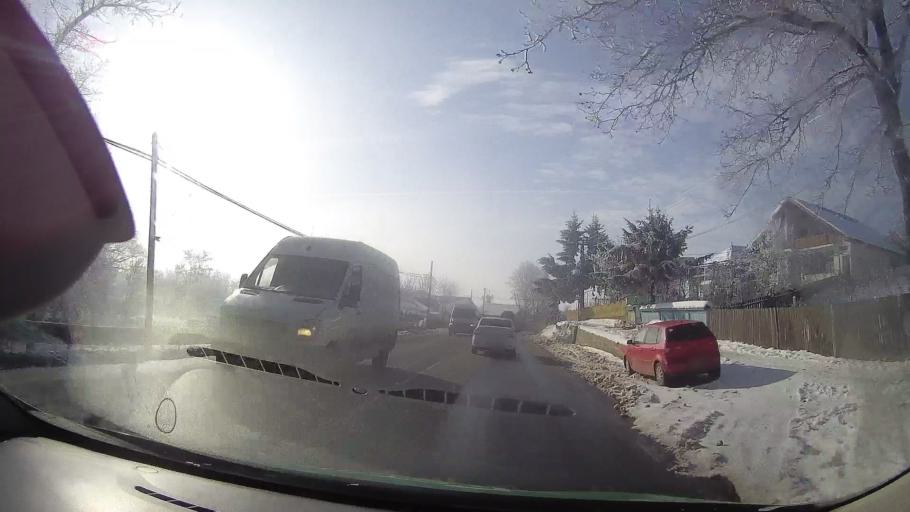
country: RO
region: Iasi
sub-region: Comuna Motca
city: Motca
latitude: 47.2357
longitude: 26.6036
